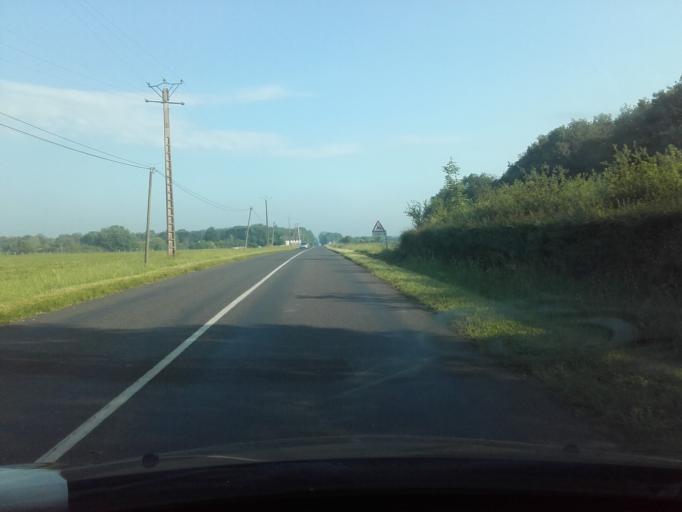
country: FR
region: Centre
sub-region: Departement d'Indre-et-Loire
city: Cinq-Mars-la-Pile
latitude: 47.3586
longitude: 0.4419
